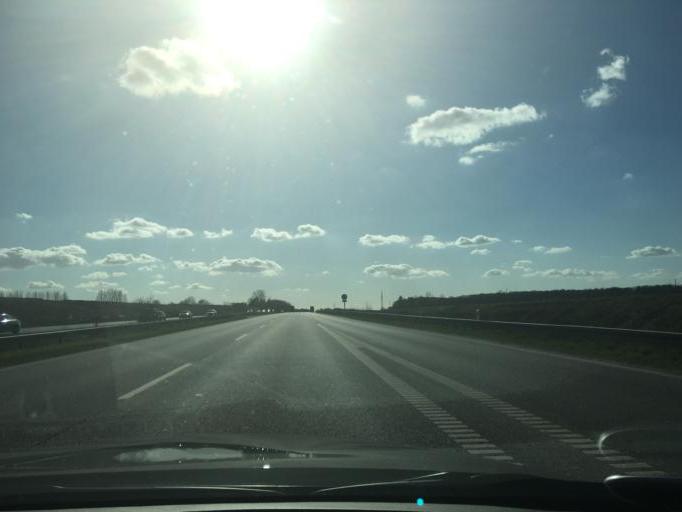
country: DK
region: Zealand
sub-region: Koge Kommune
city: Bjaeverskov
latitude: 55.4678
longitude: 12.0602
